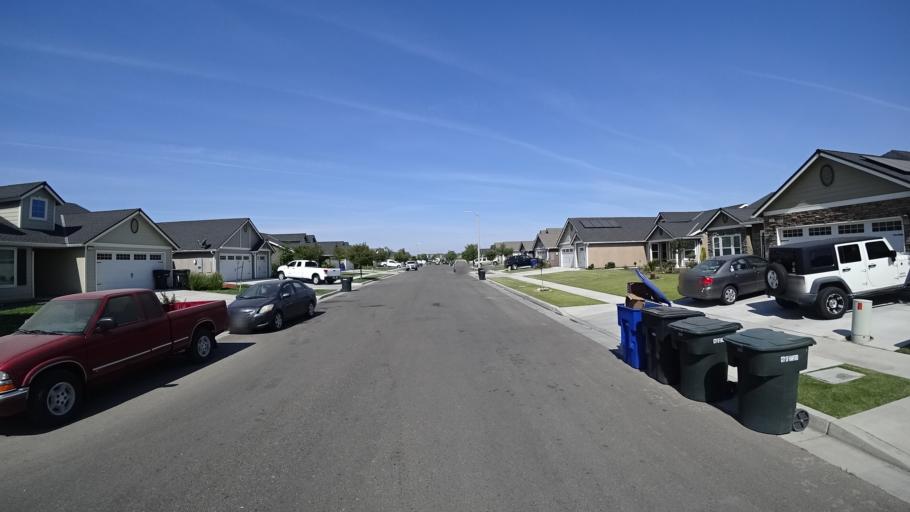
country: US
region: California
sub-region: Kings County
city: Hanford
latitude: 36.3387
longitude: -119.6741
